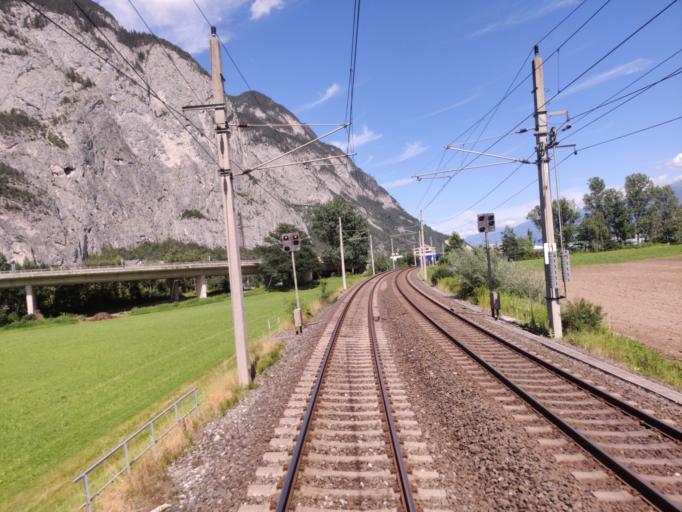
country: AT
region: Tyrol
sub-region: Politischer Bezirk Innsbruck Land
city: Unterperfuss
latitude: 47.2635
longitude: 11.2606
